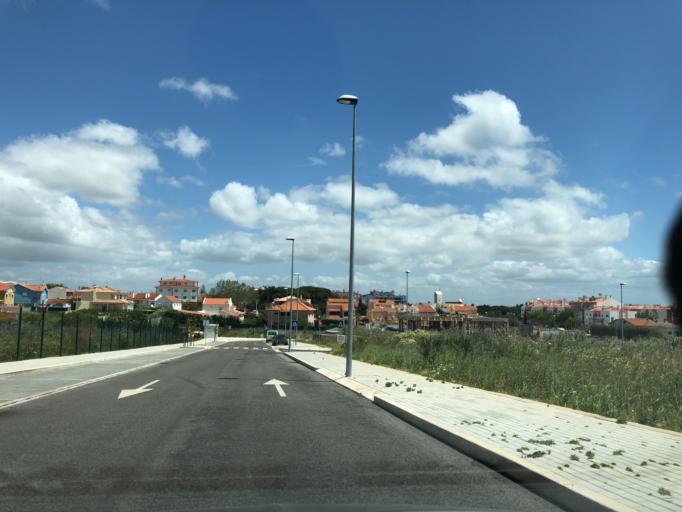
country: PT
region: Lisbon
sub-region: Cascais
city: Sao Domingos de Rana
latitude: 38.7054
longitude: -9.3287
